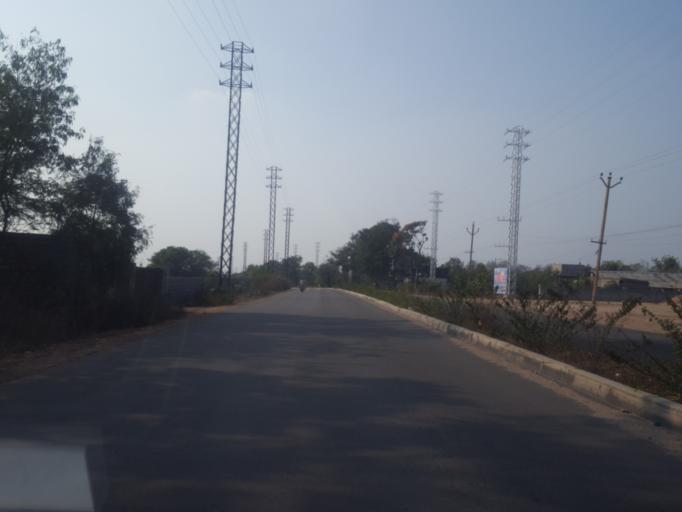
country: IN
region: Telangana
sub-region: Medak
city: Serilingampalle
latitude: 17.4154
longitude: 78.2604
